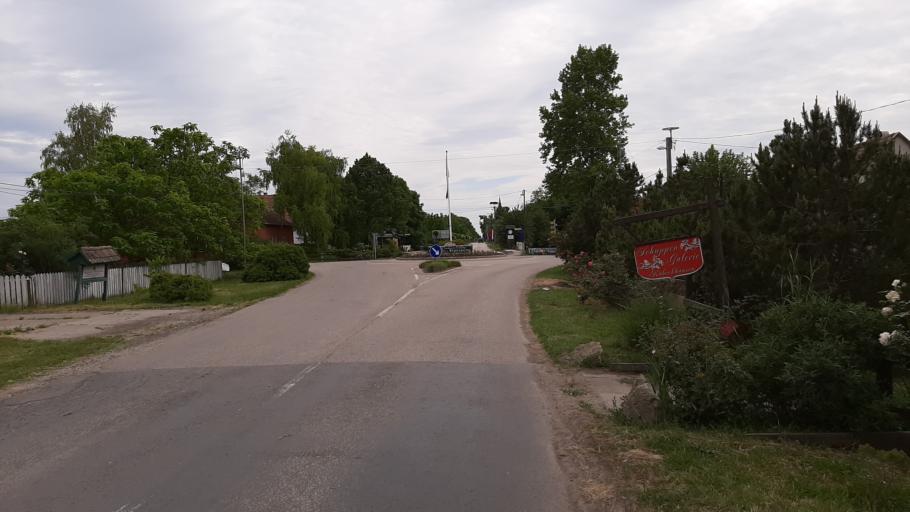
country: RO
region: Timis
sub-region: Comuna Beba Veche
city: Beba Veche
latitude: 46.1547
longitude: 20.2783
